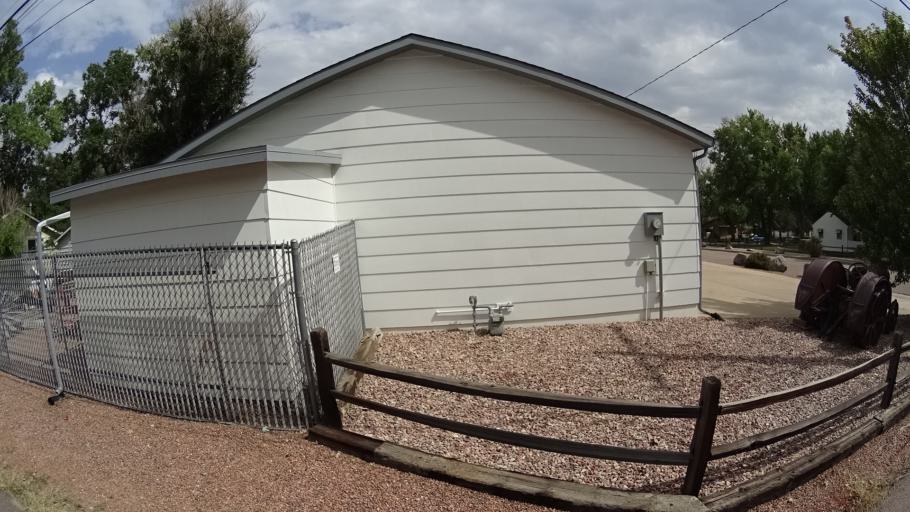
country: US
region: Colorado
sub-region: El Paso County
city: Colorado Springs
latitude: 38.8464
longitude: -104.7894
